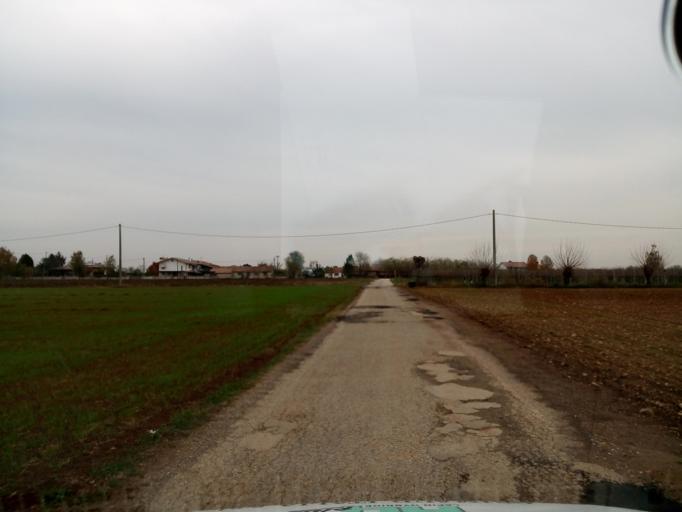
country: IT
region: Veneto
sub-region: Provincia di Treviso
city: Trevignano
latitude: 45.7239
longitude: 12.0562
